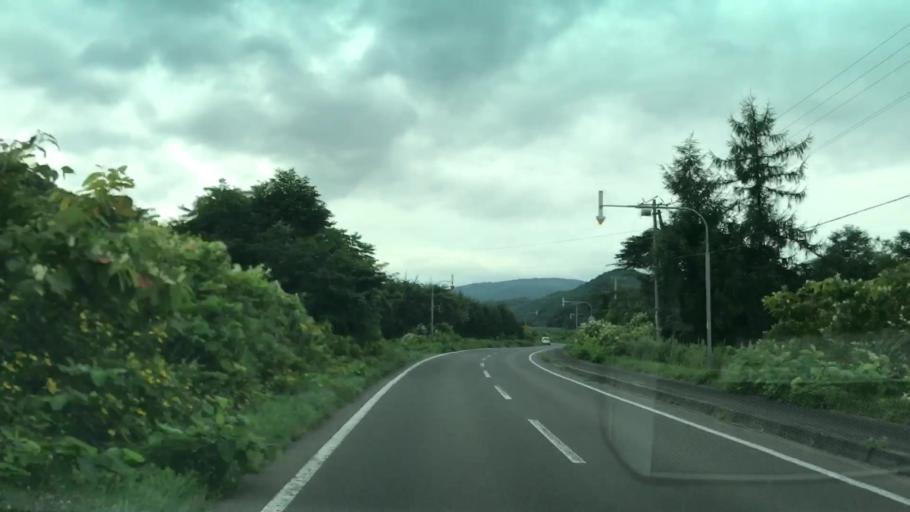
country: JP
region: Hokkaido
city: Yoichi
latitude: 43.1633
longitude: 140.8215
